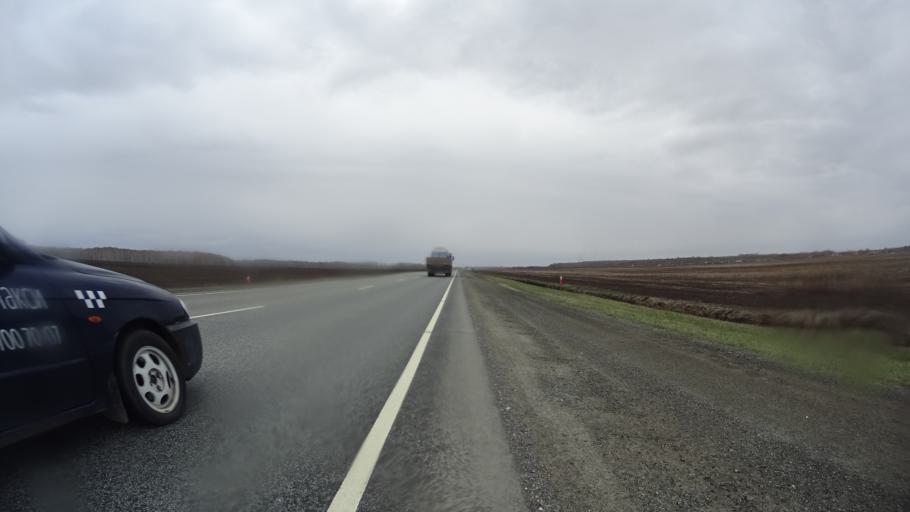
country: RU
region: Chelyabinsk
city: Krasnogorskiy
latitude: 54.5858
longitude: 61.2908
